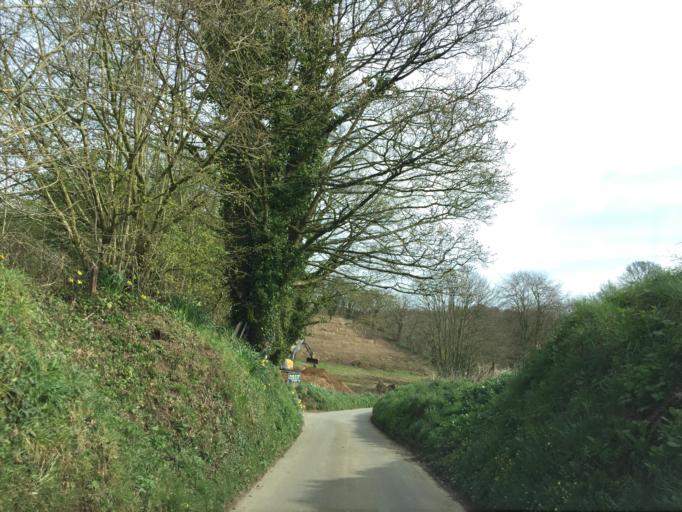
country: JE
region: St Helier
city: Saint Helier
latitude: 49.2255
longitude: -2.1354
